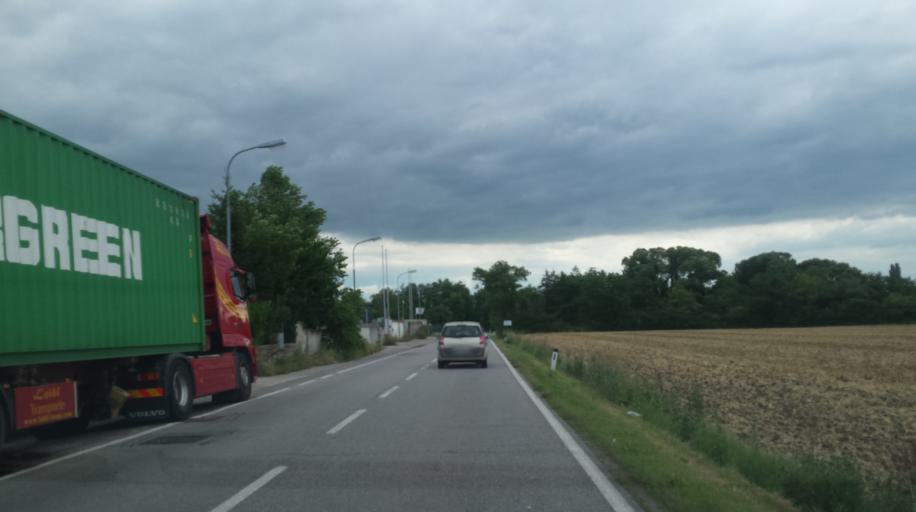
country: AT
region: Lower Austria
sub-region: Politischer Bezirk Wien-Umgebung
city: Zwolfaxing
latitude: 48.1158
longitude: 16.4569
